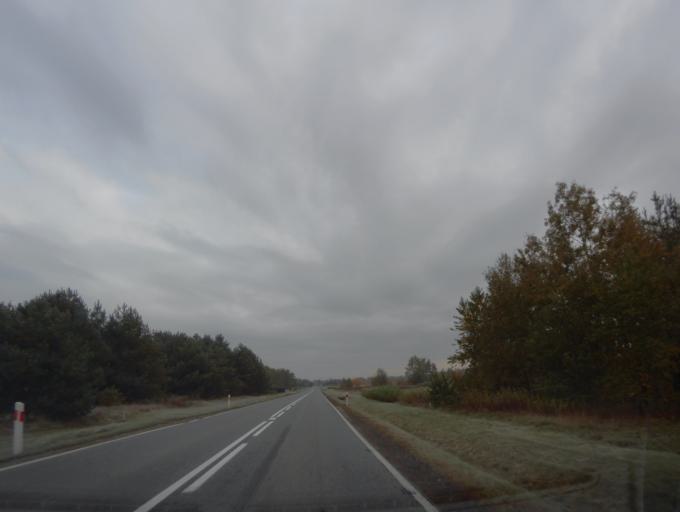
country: PL
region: Subcarpathian Voivodeship
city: Nowa Sarzyna
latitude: 50.3567
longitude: 22.3200
